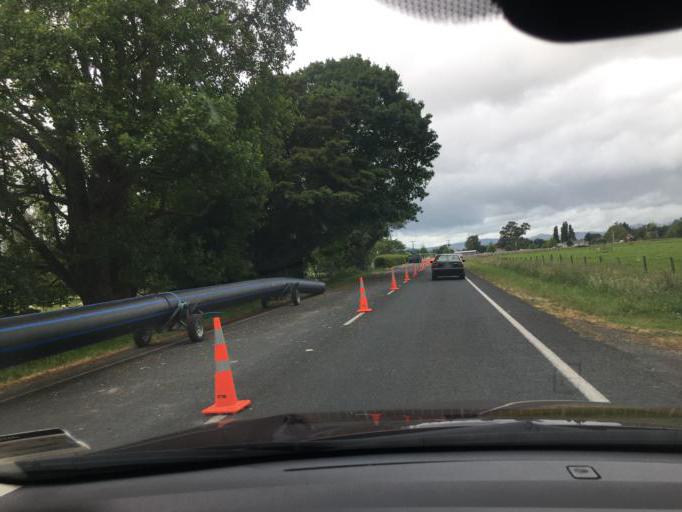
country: NZ
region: Waikato
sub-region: Waipa District
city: Cambridge
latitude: -37.9209
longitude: 175.4369
